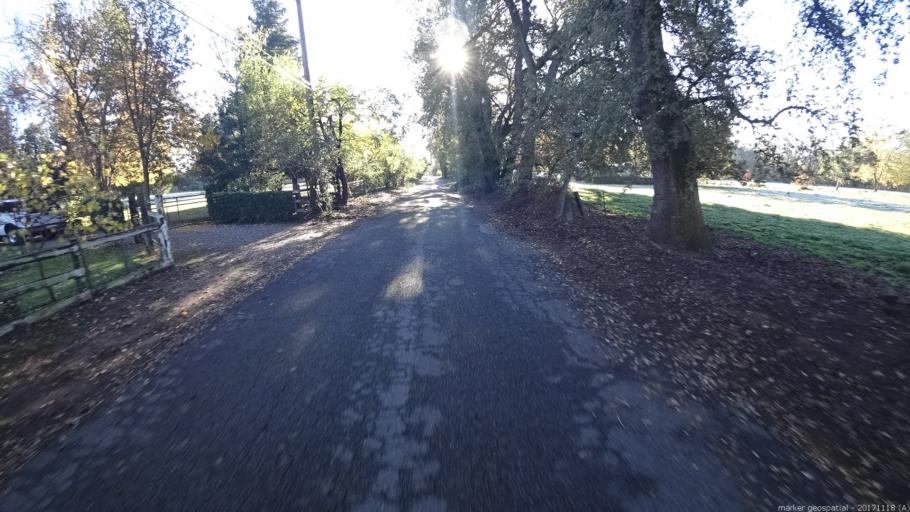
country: US
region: California
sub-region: Shasta County
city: Anderson
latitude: 40.4488
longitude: -122.2787
